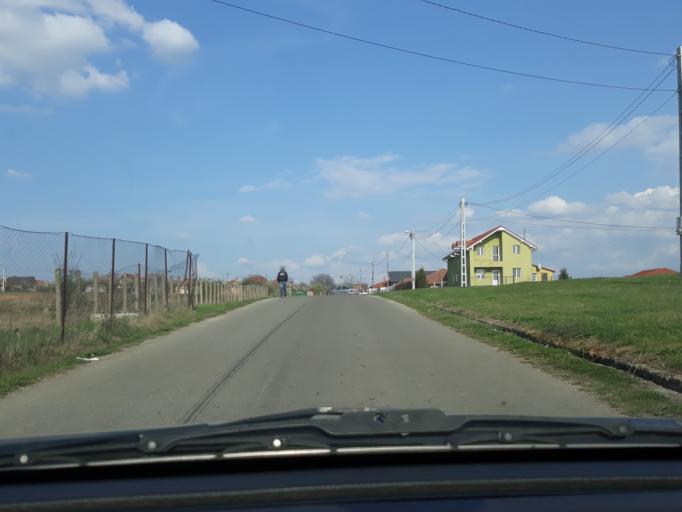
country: RO
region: Bihor
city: Margita
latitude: 47.3506
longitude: 22.3287
